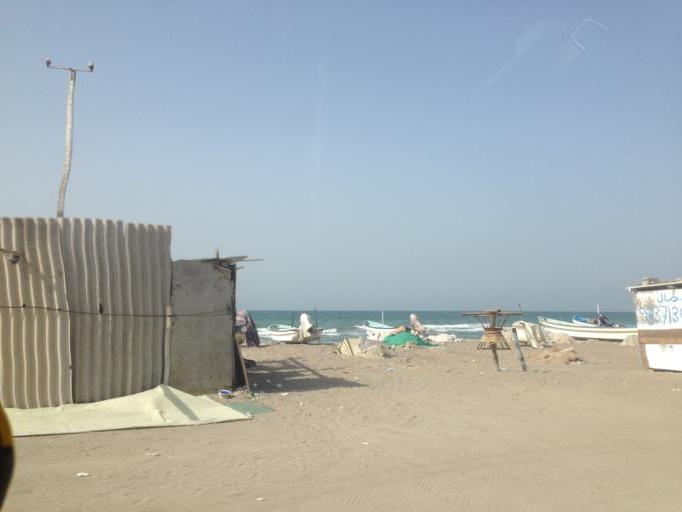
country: OM
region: Al Batinah
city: Barka'
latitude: 23.7077
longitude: 57.9290
